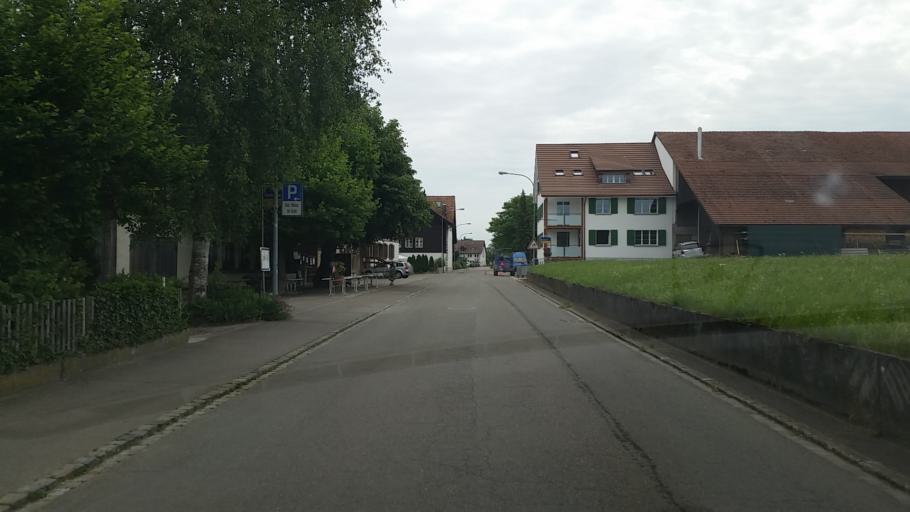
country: CH
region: Zurich
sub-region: Bezirk Dielsdorf
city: Otelfingen
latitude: 47.4981
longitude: 8.3917
